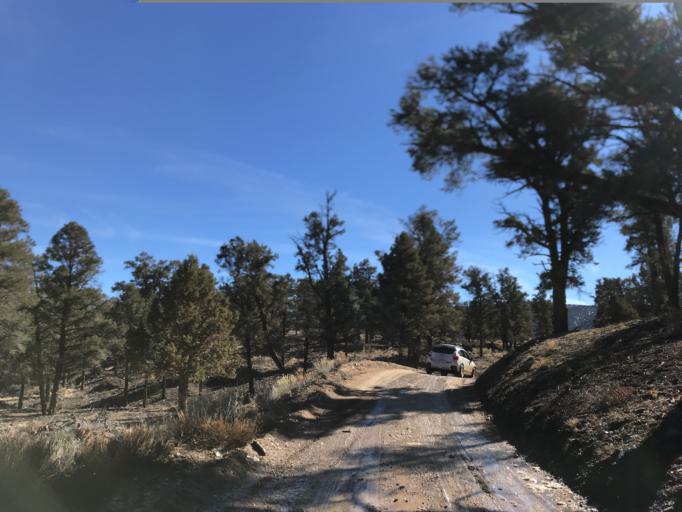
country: US
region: California
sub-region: San Bernardino County
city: Big Bear City
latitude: 34.2614
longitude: -116.7528
